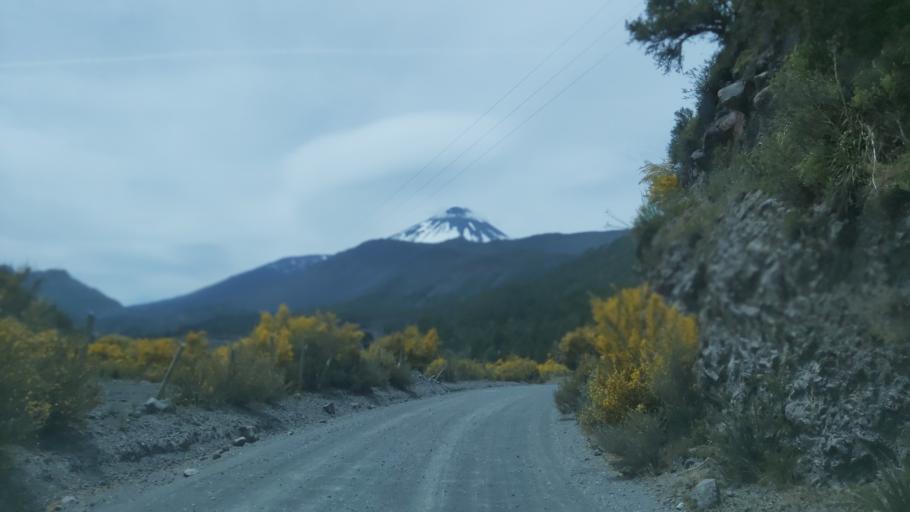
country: AR
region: Neuquen
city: Andacollo
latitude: -37.3979
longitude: -71.4447
